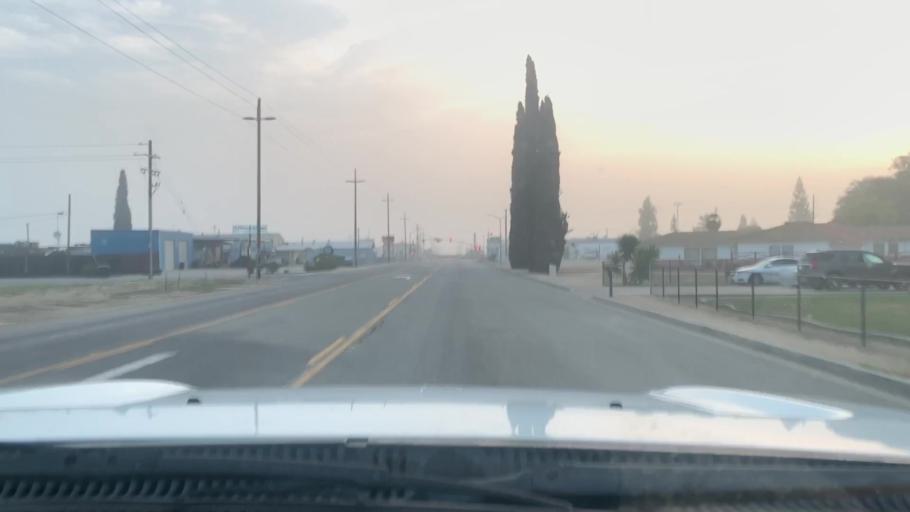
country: US
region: California
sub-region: Kern County
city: Wasco
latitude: 35.6015
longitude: -119.3366
